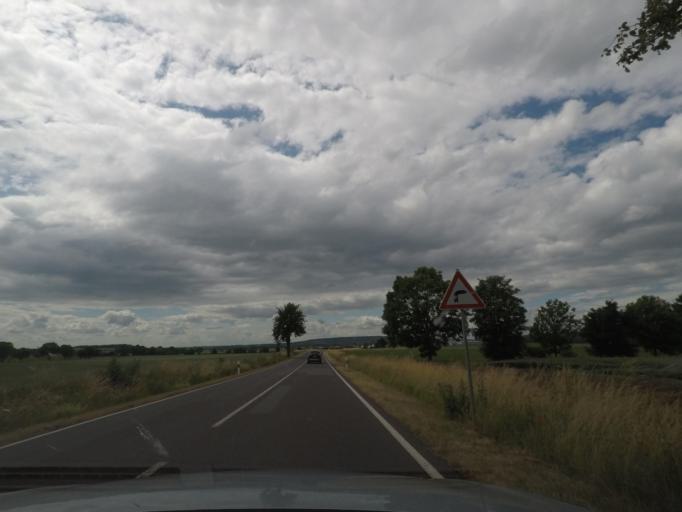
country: DE
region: Saxony-Anhalt
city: Hotensleben
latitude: 52.1064
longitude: 11.0408
